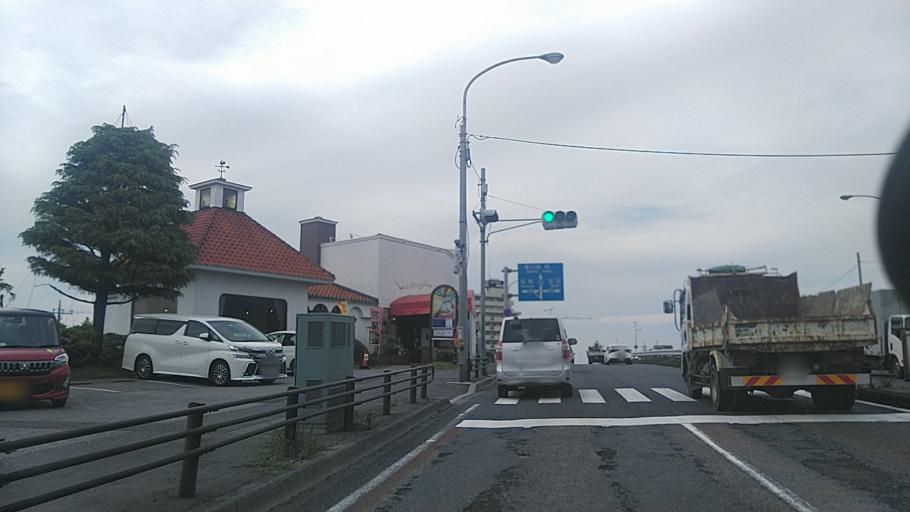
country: JP
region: Chiba
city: Yotsukaido
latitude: 35.7135
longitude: 140.1183
